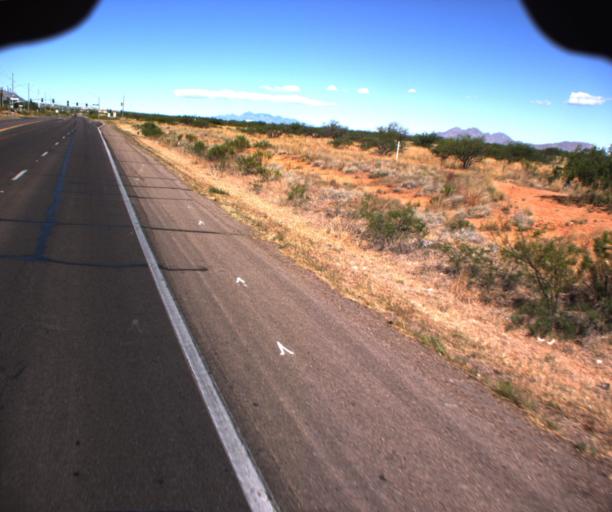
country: US
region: Arizona
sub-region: Cochise County
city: Sierra Vista
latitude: 31.5695
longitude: -110.2888
